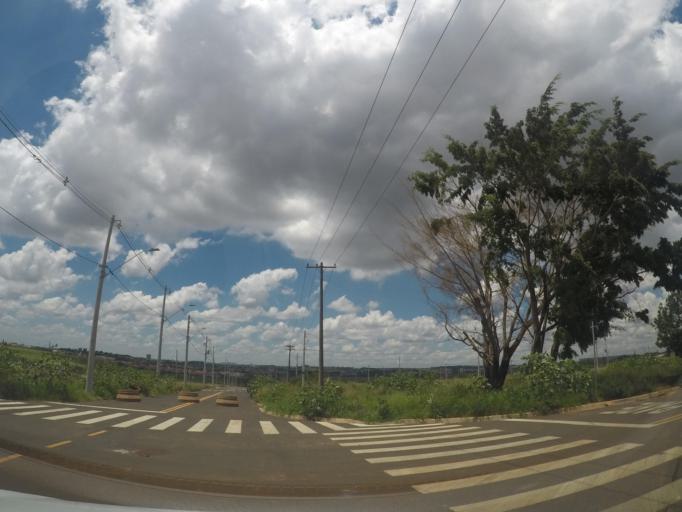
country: BR
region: Sao Paulo
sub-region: Hortolandia
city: Hortolandia
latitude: -22.8399
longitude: -47.2349
